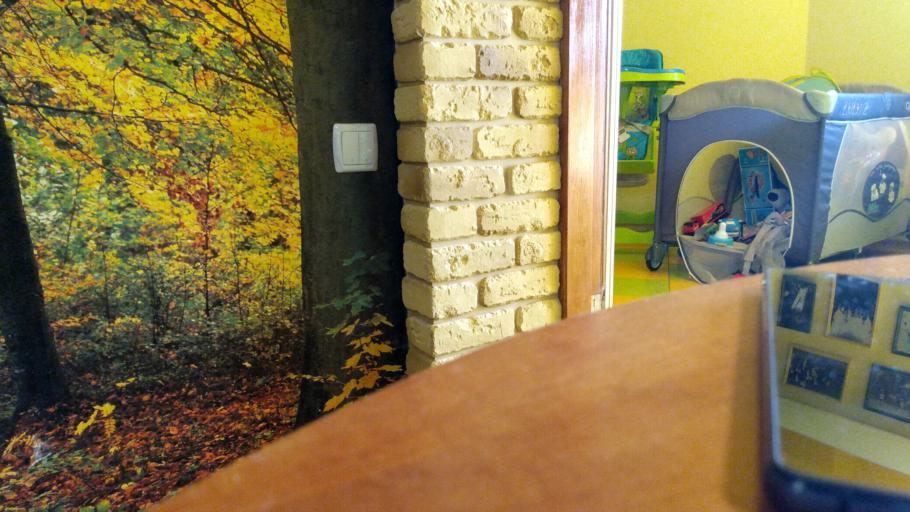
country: RU
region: Tverskaya
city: Kalashnikovo
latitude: 57.3793
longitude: 35.1951
